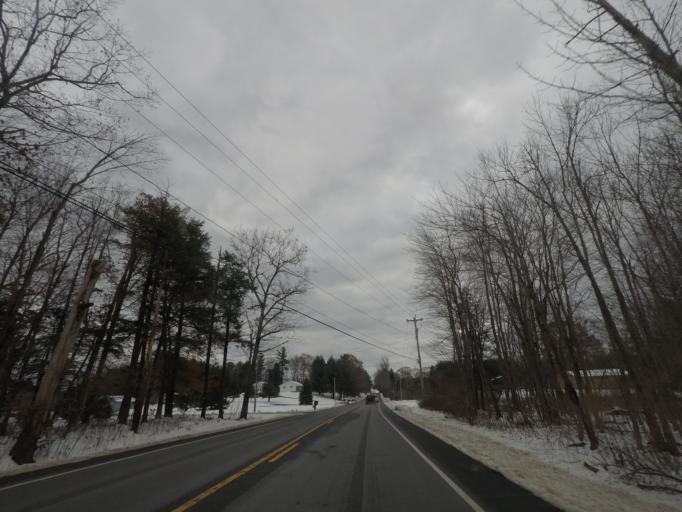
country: US
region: New York
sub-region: Rensselaer County
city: West Sand Lake
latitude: 42.6198
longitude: -73.6035
